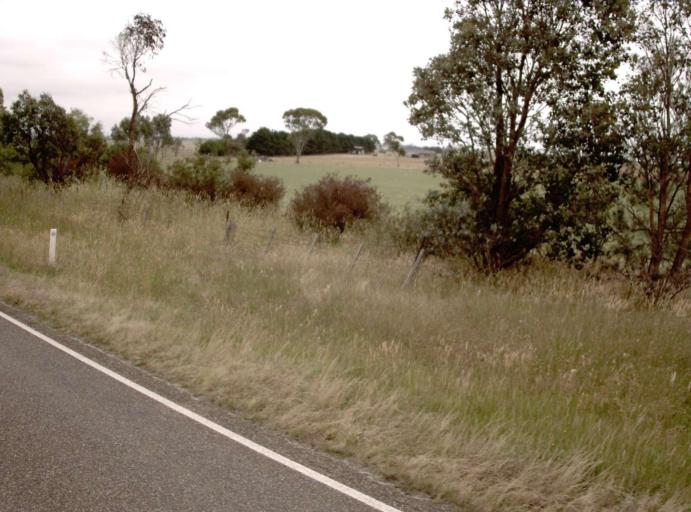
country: AU
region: Victoria
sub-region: Wellington
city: Heyfield
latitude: -38.1106
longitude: 146.7712
